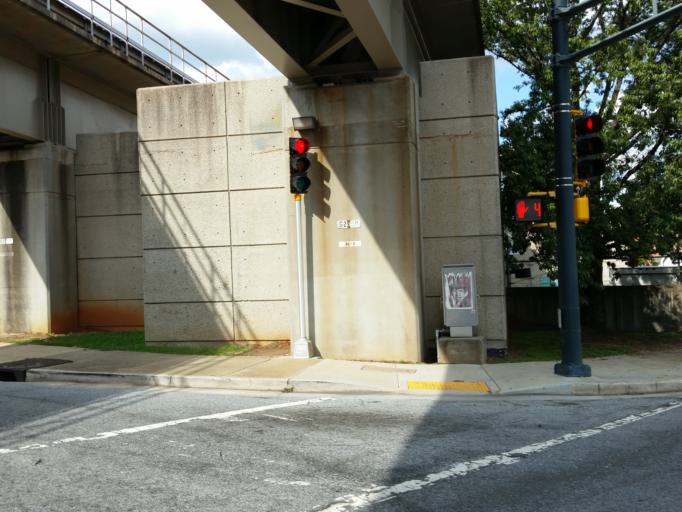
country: US
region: Georgia
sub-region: Fulton County
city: Atlanta
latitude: 33.7470
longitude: -84.3969
